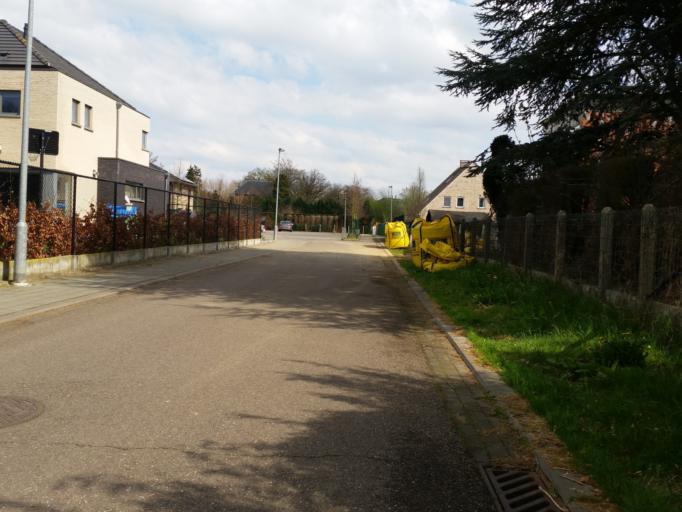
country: BE
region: Flanders
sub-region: Provincie Vlaams-Brabant
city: Haacht
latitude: 50.9362
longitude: 4.6201
